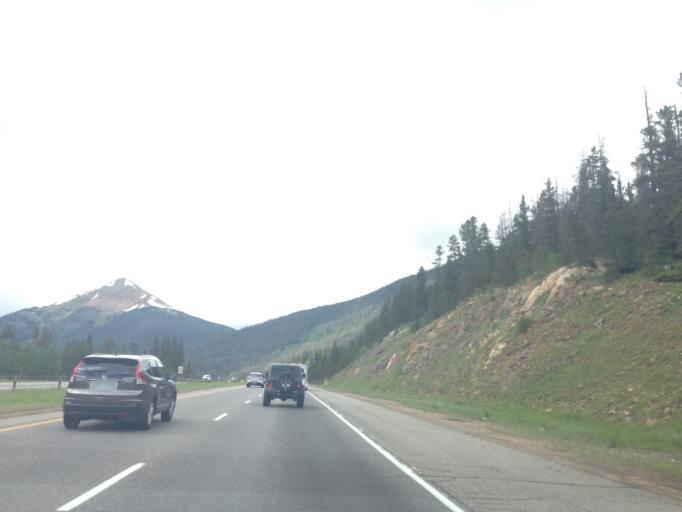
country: US
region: Colorado
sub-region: Clear Creek County
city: Georgetown
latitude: 39.6973
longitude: -105.8305
